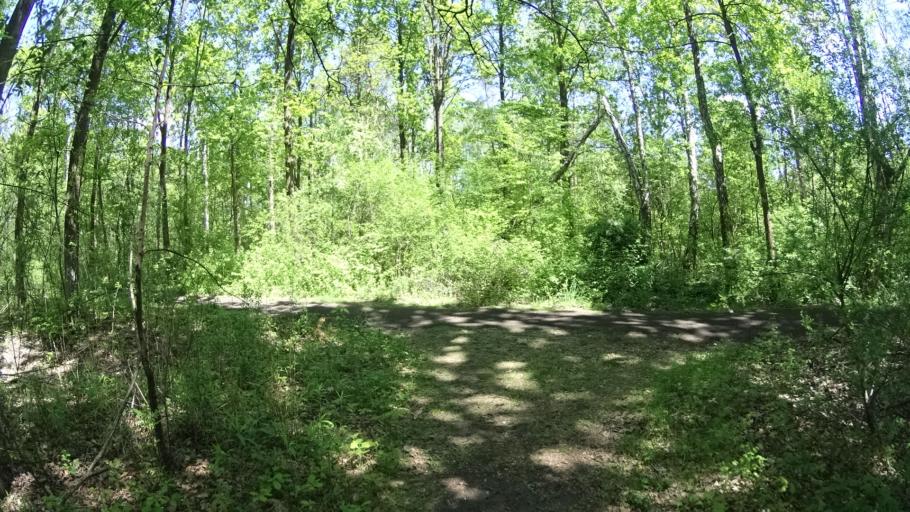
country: PL
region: Masovian Voivodeship
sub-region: Warszawa
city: Bemowo
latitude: 52.2709
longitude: 20.8843
